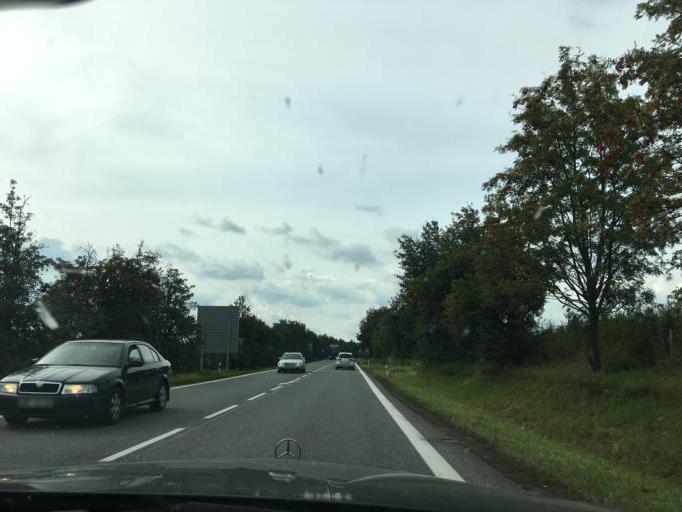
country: CZ
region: Kralovehradecky
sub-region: Okres Nachod
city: Ceska Skalice
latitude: 50.3911
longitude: 15.9963
